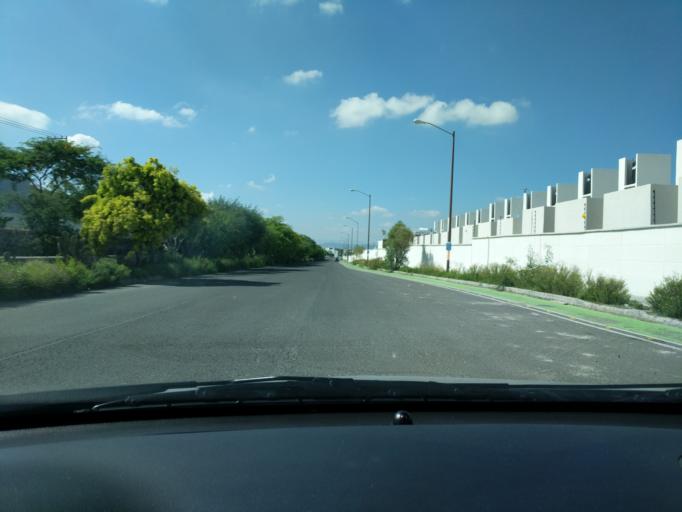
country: MX
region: Queretaro
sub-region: Queretaro
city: Patria Nueva
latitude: 20.6378
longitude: -100.4901
